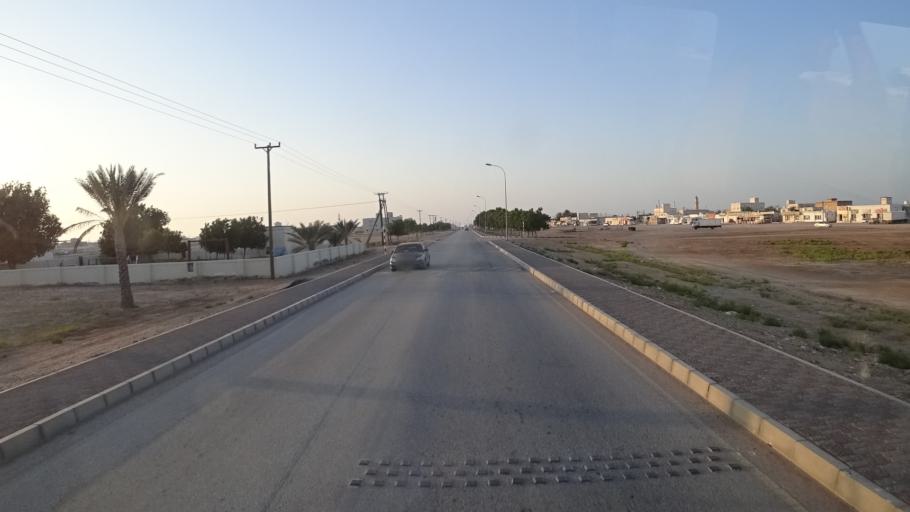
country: OM
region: Ash Sharqiyah
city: Sur
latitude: 22.5166
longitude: 59.7932
